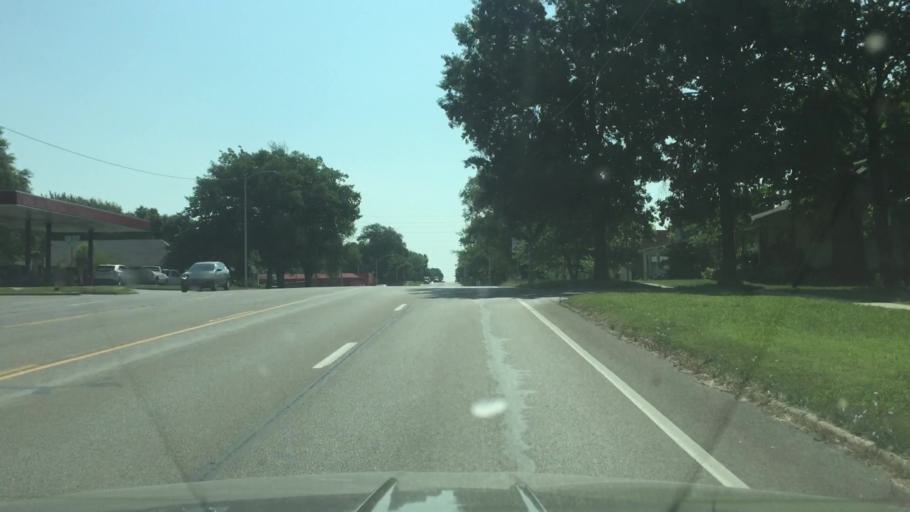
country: US
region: Missouri
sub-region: Pettis County
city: Sedalia
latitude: 38.7034
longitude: -93.2090
